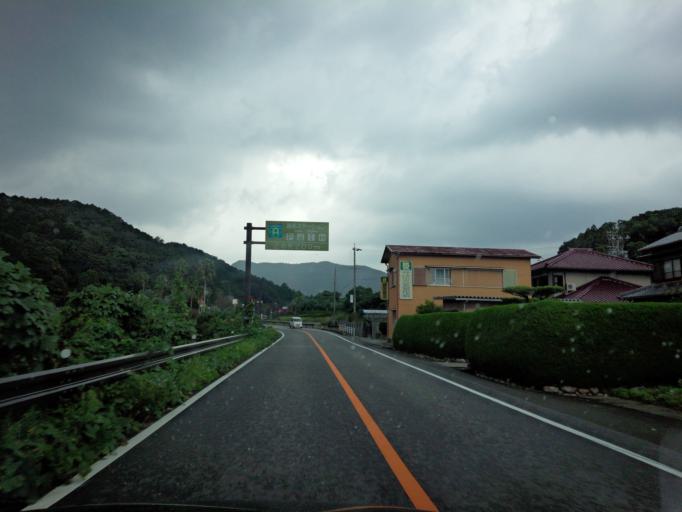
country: JP
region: Mie
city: Toba
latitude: 34.3858
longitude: 136.7977
